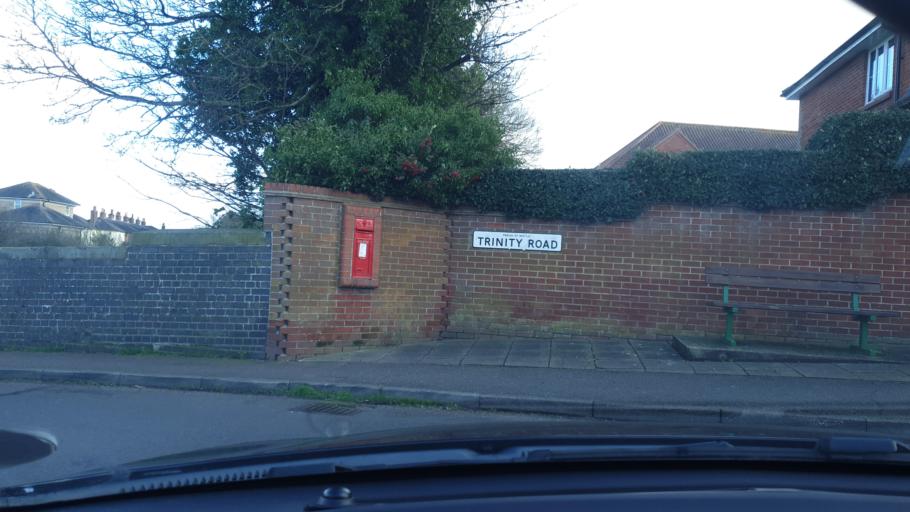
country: GB
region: England
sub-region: Essex
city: Manningtree
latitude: 51.9427
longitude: 1.0631
